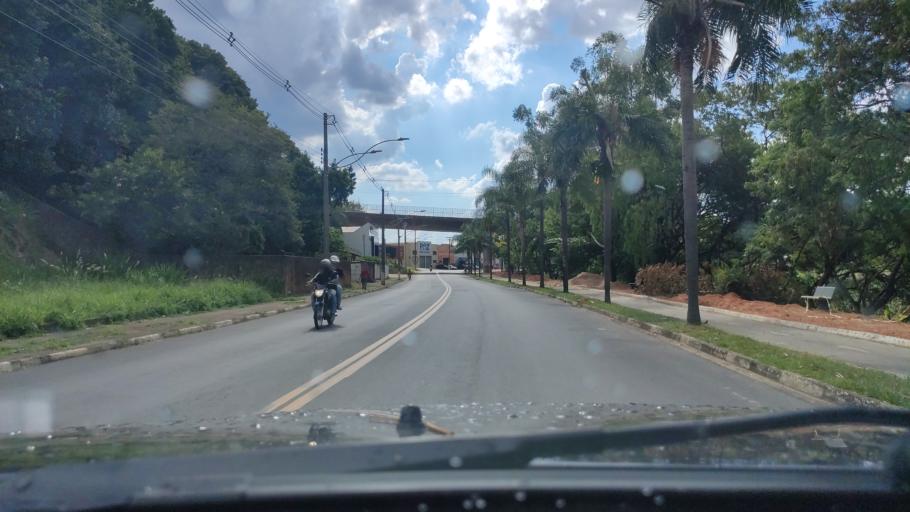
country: BR
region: Sao Paulo
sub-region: Itapira
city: Itapira
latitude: -22.4352
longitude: -46.8191
